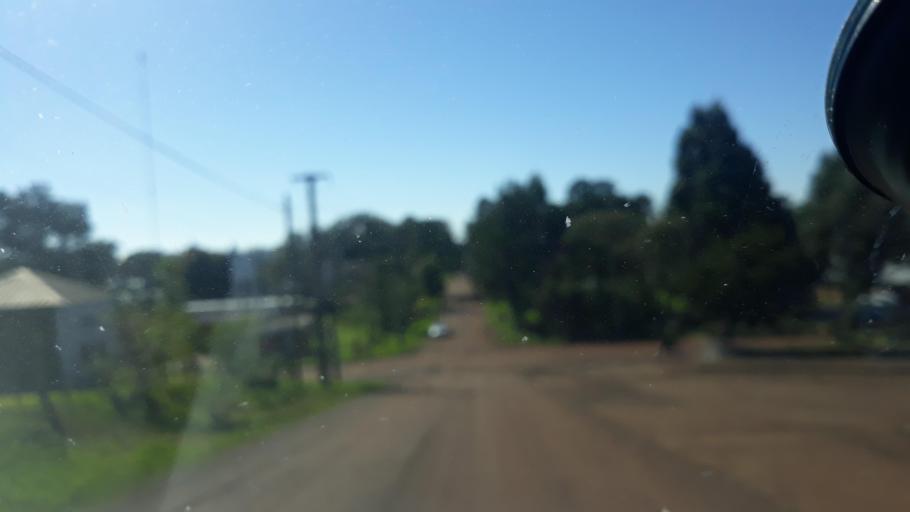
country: AR
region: Misiones
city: Bernardo de Irigoyen
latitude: -26.2627
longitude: -53.6490
